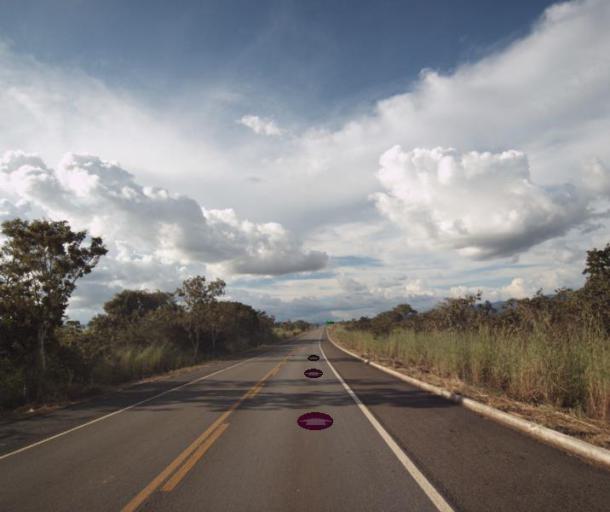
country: BR
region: Goias
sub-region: Barro Alto
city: Barro Alto
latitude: -14.8227
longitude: -48.6382
